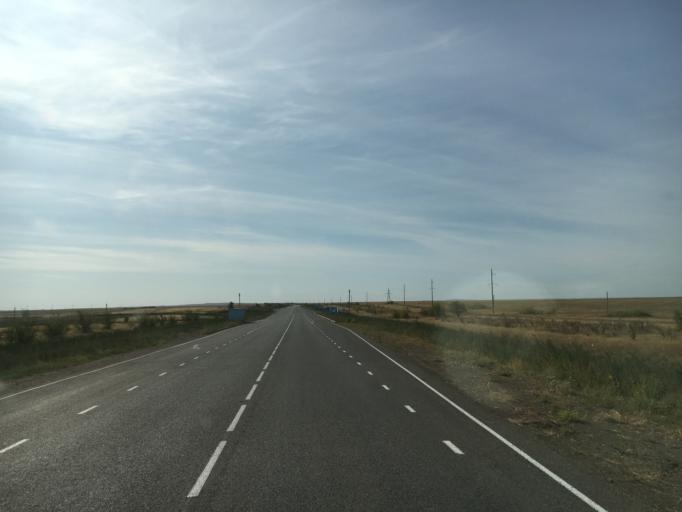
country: KZ
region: Batys Qazaqstan
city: Peremetnoe
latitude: 51.1202
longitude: 50.7442
